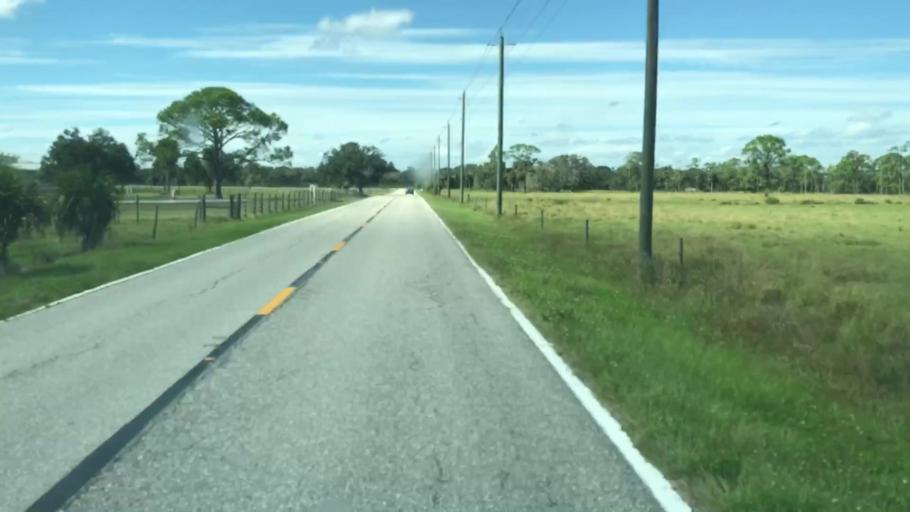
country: US
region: Florida
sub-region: Lee County
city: Alva
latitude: 26.7230
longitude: -81.6179
